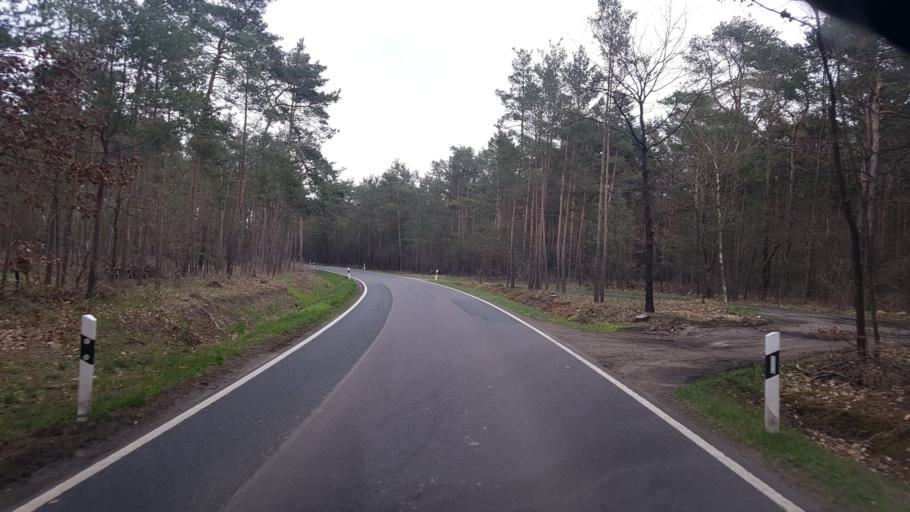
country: DE
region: Brandenburg
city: Hohenbocka
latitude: 51.4506
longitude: 13.9766
